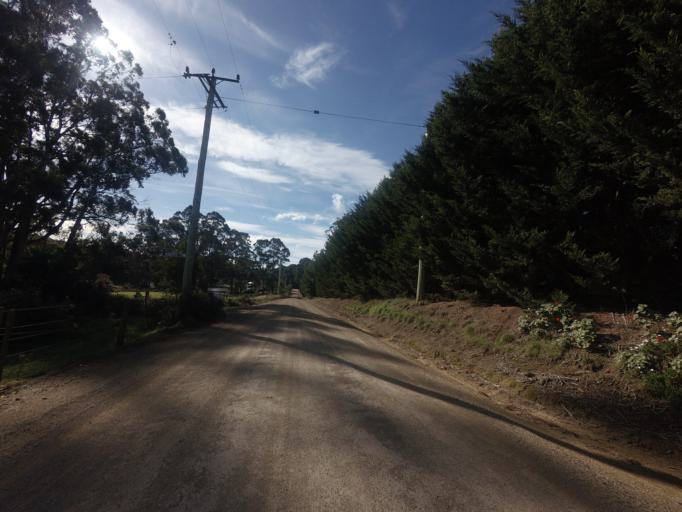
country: AU
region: Tasmania
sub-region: Clarence
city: Sandford
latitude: -43.1494
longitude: 147.7639
